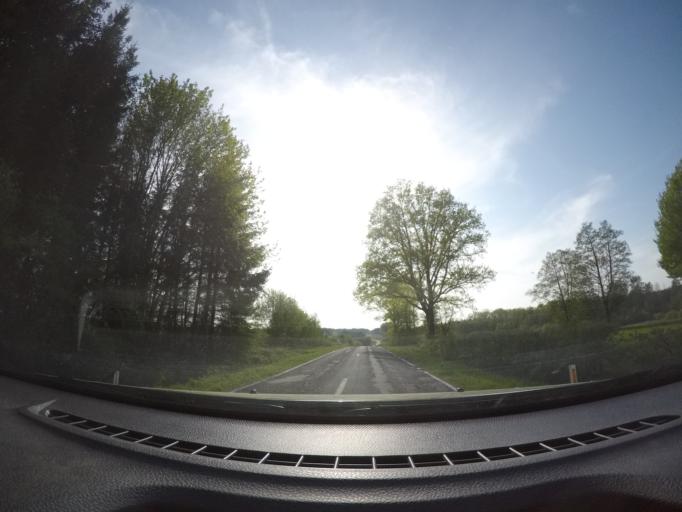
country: BE
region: Wallonia
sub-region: Province du Luxembourg
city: Tintigny
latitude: 49.6683
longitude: 5.5531
